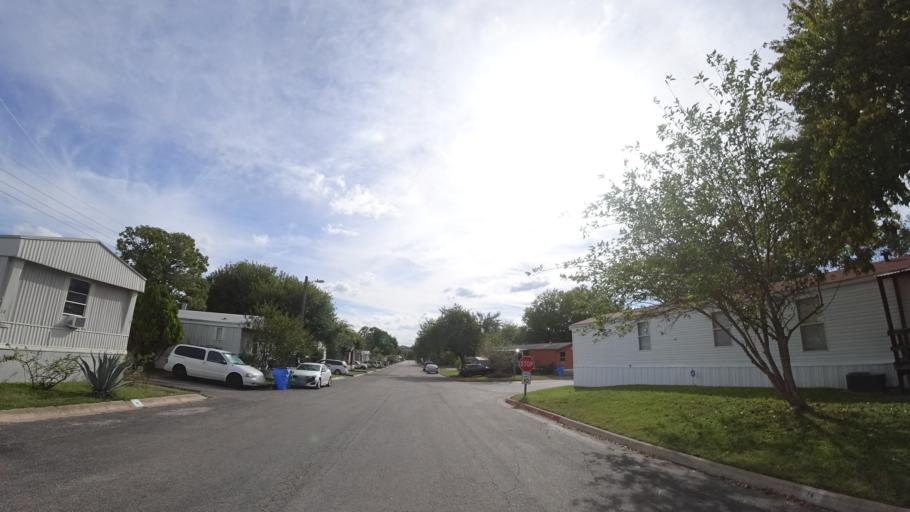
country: US
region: Texas
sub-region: Travis County
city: Austin
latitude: 30.1995
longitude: -97.7557
